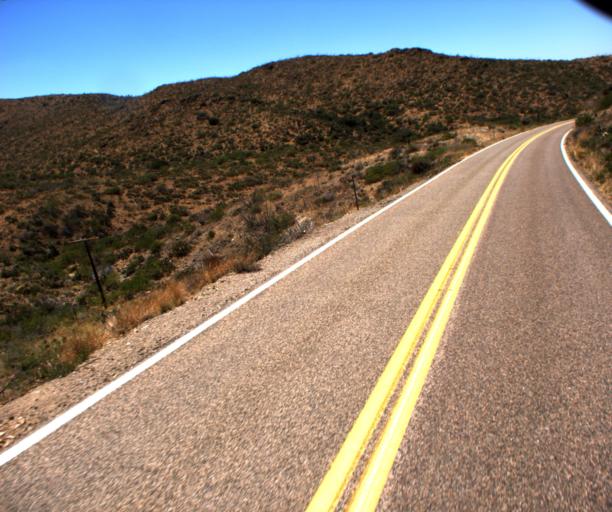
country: US
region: Arizona
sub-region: Yavapai County
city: Bagdad
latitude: 34.4468
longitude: -112.9694
